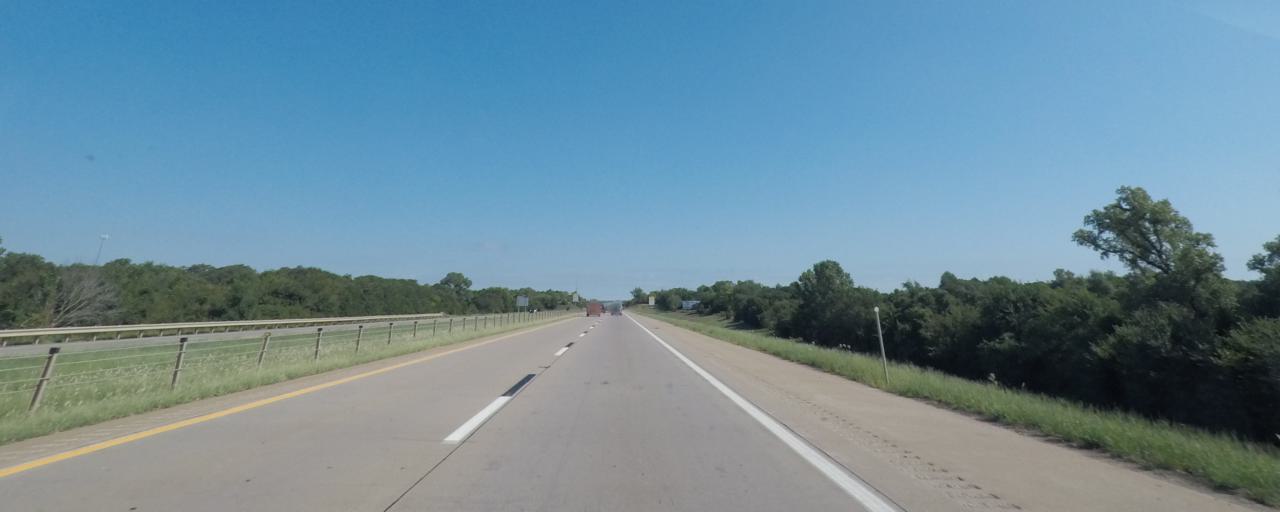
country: US
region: Oklahoma
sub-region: Oklahoma County
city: Edmond
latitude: 35.7347
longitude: -97.4162
